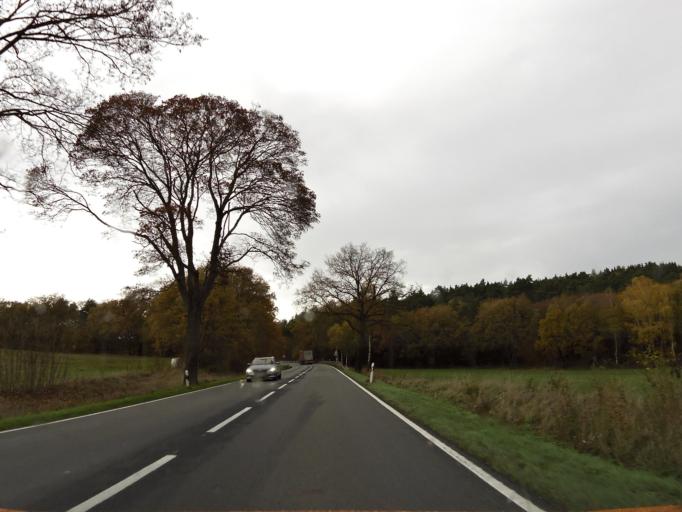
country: DE
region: Saxony-Anhalt
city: Kalbe
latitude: 52.6202
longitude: 11.3178
